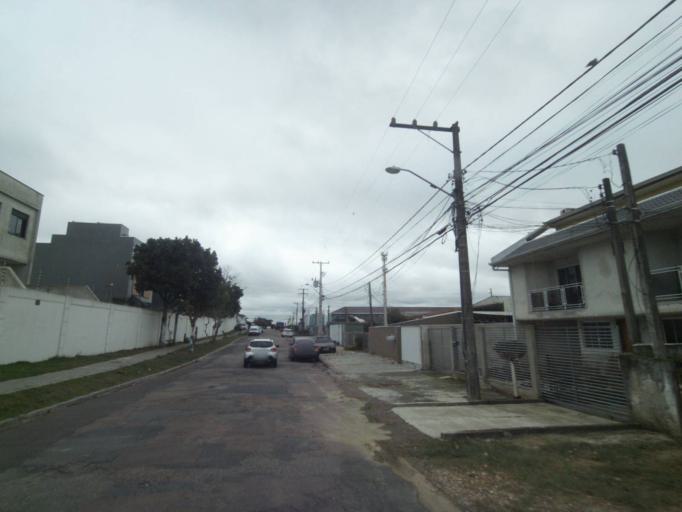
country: BR
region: Parana
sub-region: Curitiba
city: Curitiba
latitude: -25.5179
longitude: -49.3029
